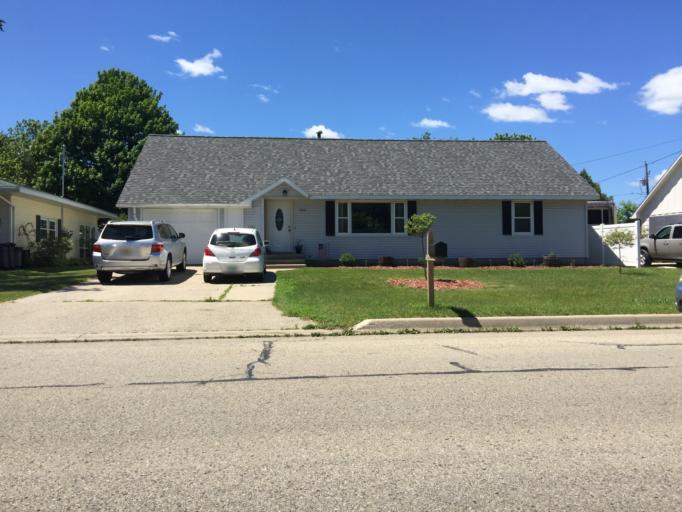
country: US
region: Michigan
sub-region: Menominee County
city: Menominee
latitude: 45.1373
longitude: -87.6176
